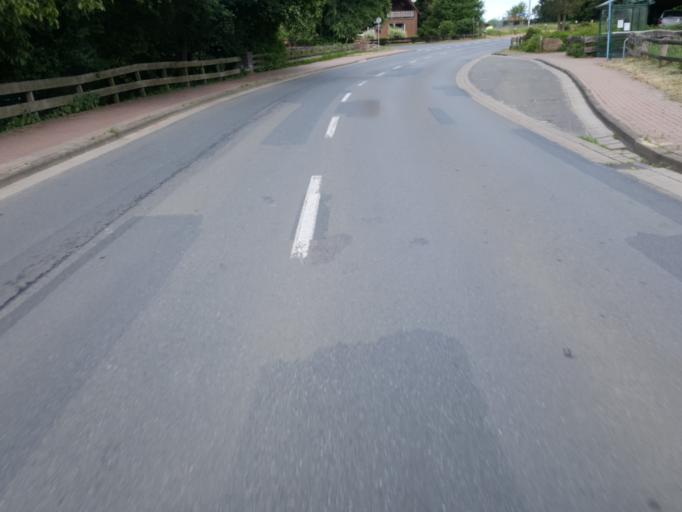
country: DE
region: Lower Saxony
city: Husum
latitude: 52.5966
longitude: 9.2454
